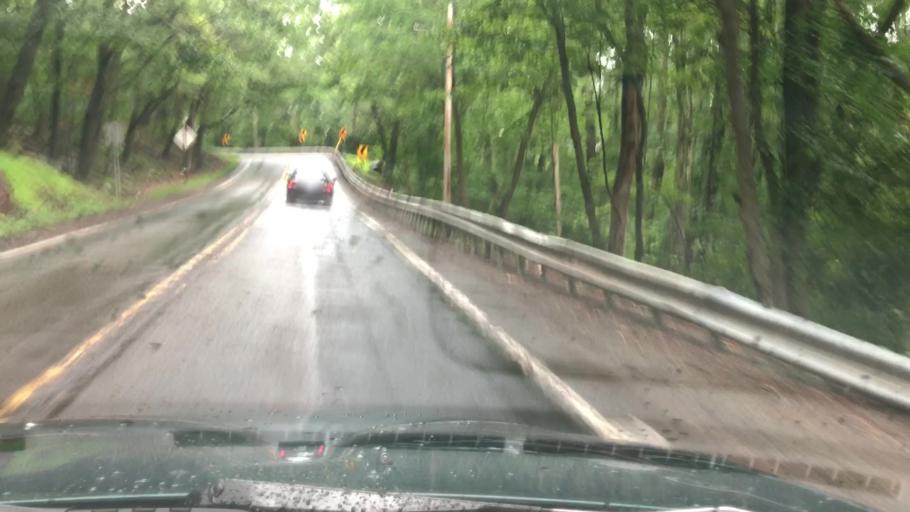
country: US
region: Pennsylvania
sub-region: Monroe County
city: Mountainhome
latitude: 41.2407
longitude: -75.2324
